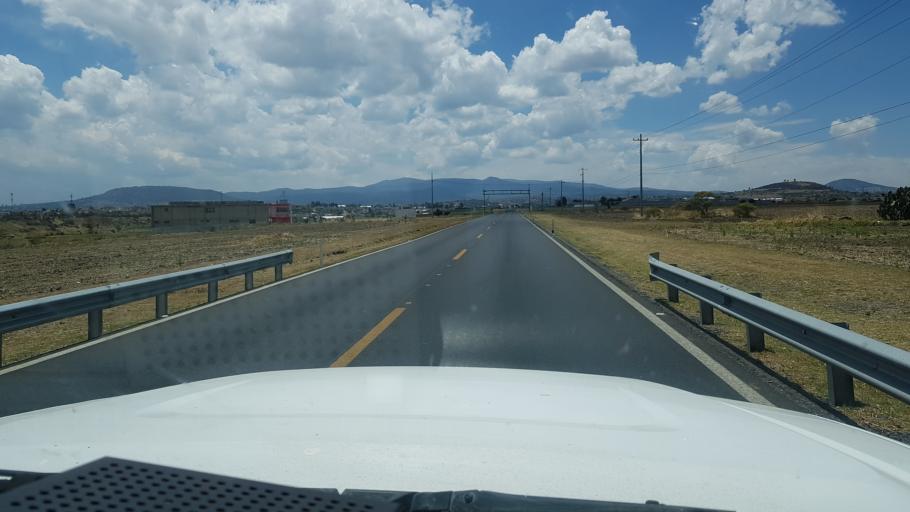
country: MX
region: Hidalgo
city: Calpulalpan
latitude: 19.6071
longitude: -98.5617
